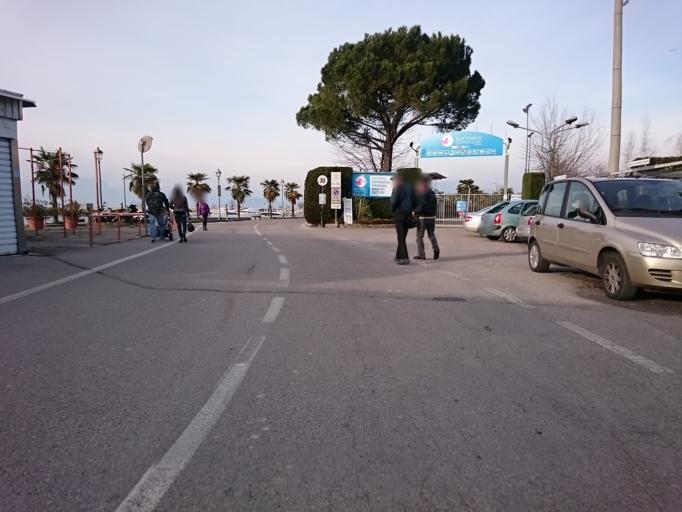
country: IT
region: Veneto
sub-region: Provincia di Verona
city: Peschiera del Garda
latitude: 45.4449
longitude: 10.6945
